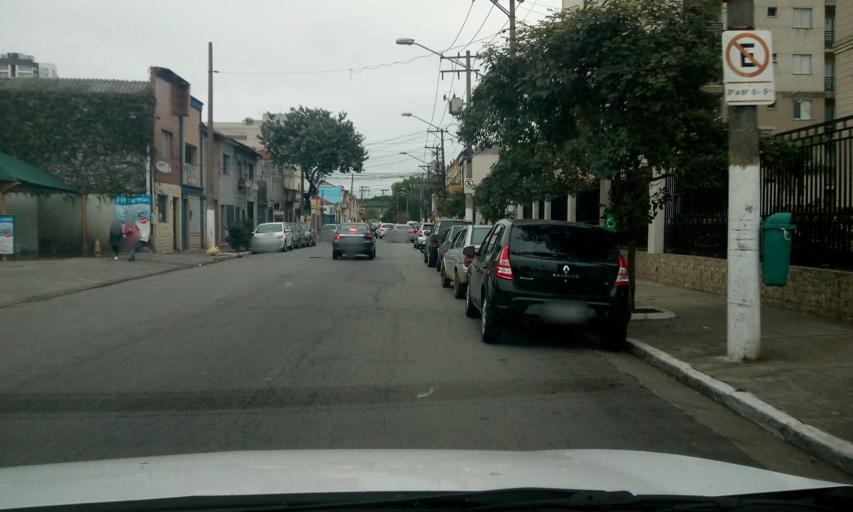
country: BR
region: Sao Paulo
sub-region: Sao Paulo
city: Sao Paulo
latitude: -23.5458
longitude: -46.5926
